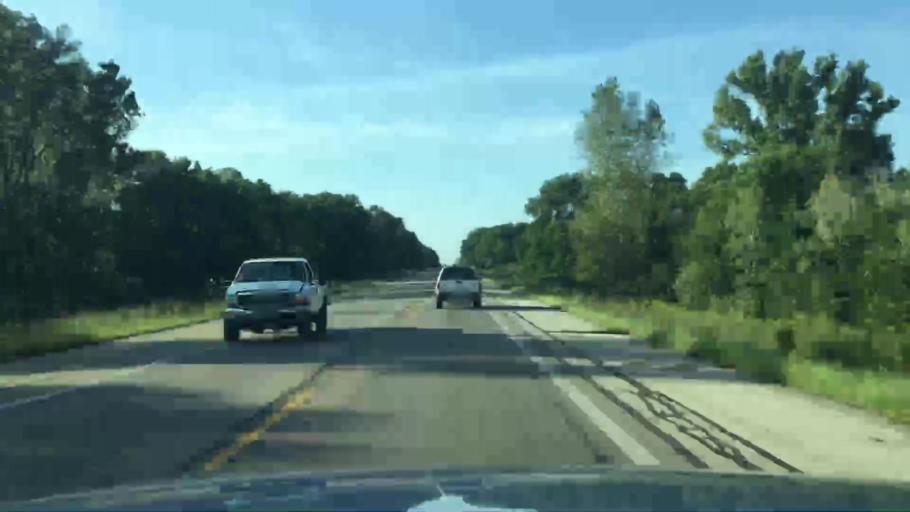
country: US
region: Michigan
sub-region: Jackson County
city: Vandercook Lake
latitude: 42.0937
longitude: -84.3639
